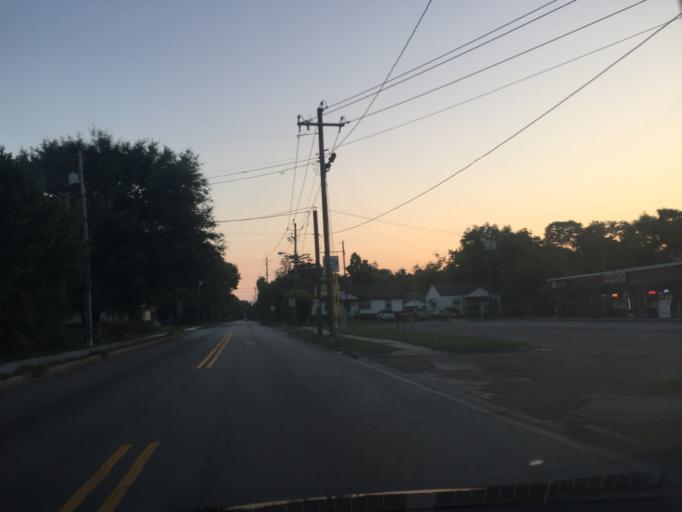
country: US
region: Georgia
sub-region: Chatham County
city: Thunderbolt
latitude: 32.0650
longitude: -81.0590
